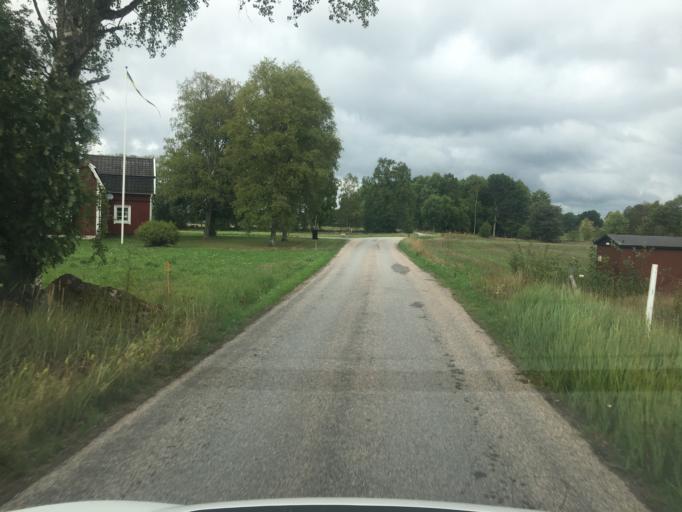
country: SE
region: Kronoberg
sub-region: Ljungby Kommun
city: Lagan
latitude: 56.9262
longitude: 14.0220
